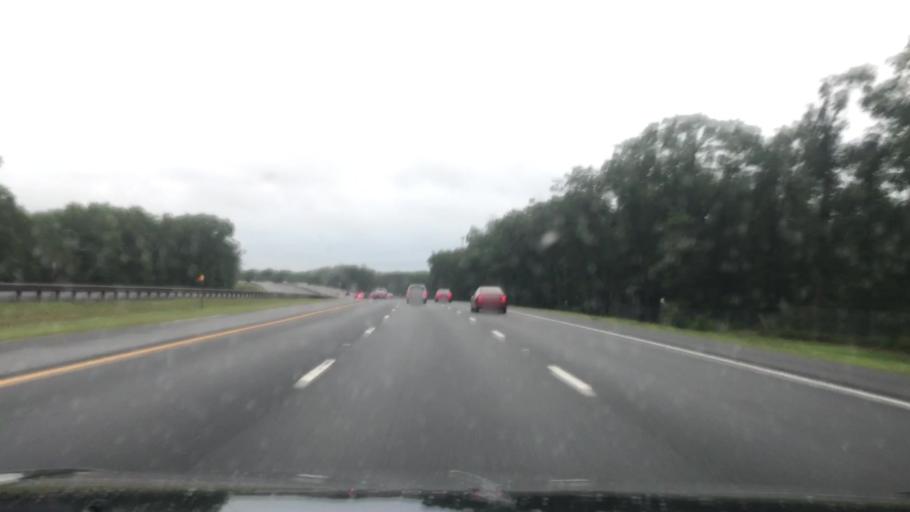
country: US
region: New Jersey
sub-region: Ocean County
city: Leisure Village East
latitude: 40.0101
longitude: -74.1900
